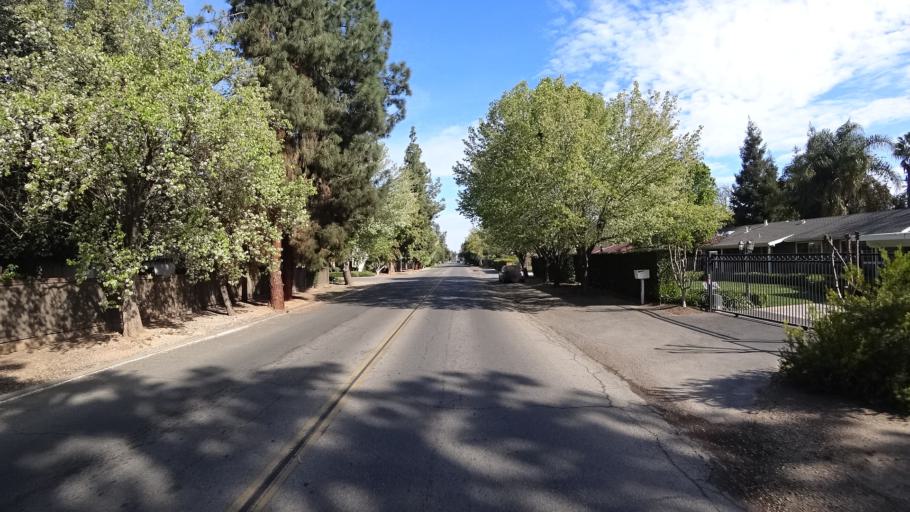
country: US
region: California
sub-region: Fresno County
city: Fresno
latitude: 36.7982
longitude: -119.7995
